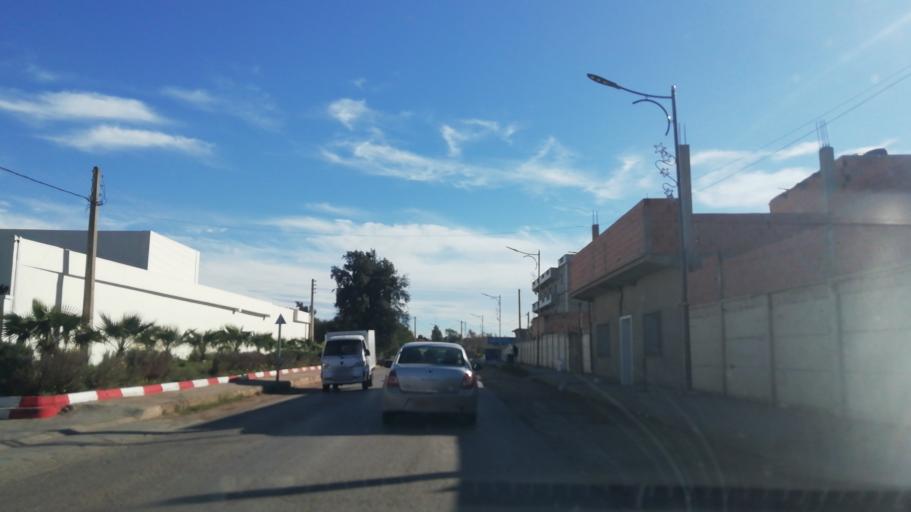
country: DZ
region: Oran
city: Es Senia
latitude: 35.6145
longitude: -0.5843
